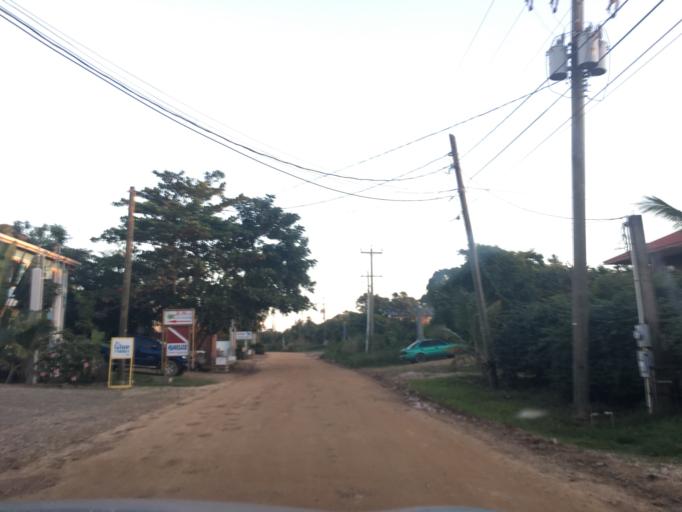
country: BZ
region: Stann Creek
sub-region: Dangriga
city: Dangriga
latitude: 16.8384
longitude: -88.2702
